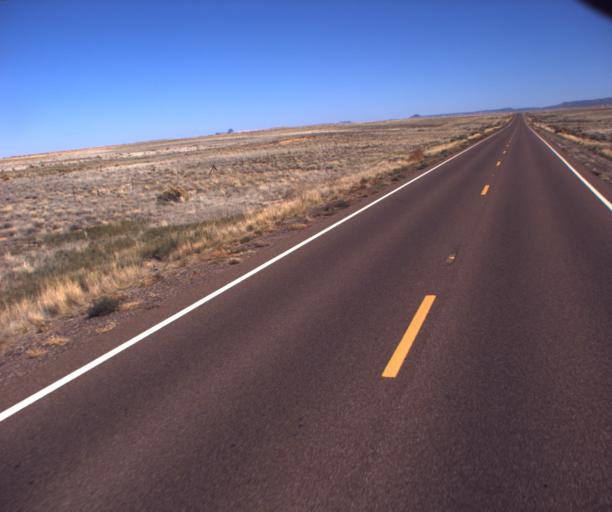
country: US
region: Arizona
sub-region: Navajo County
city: Joseph City
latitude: 35.1455
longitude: -110.4777
